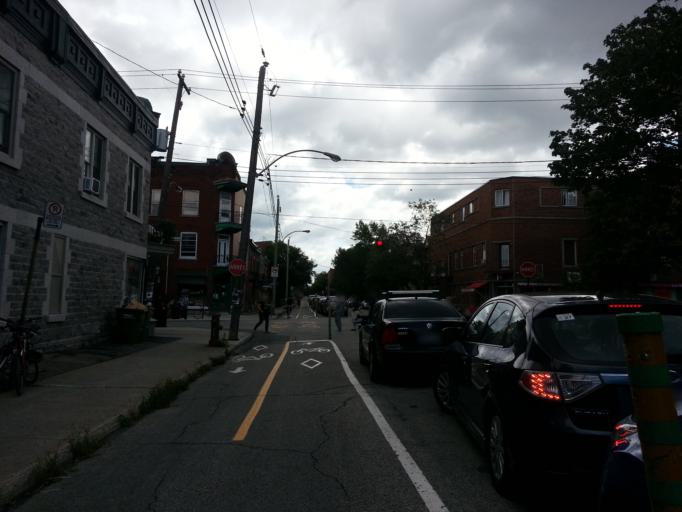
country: CA
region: Quebec
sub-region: Montreal
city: Montreal
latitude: 45.5235
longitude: -73.5954
